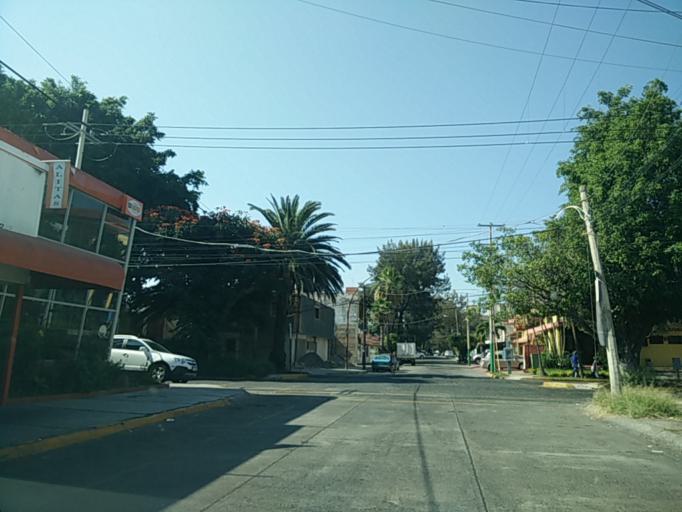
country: MX
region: Jalisco
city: Guadalajara
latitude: 20.6498
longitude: -103.3985
